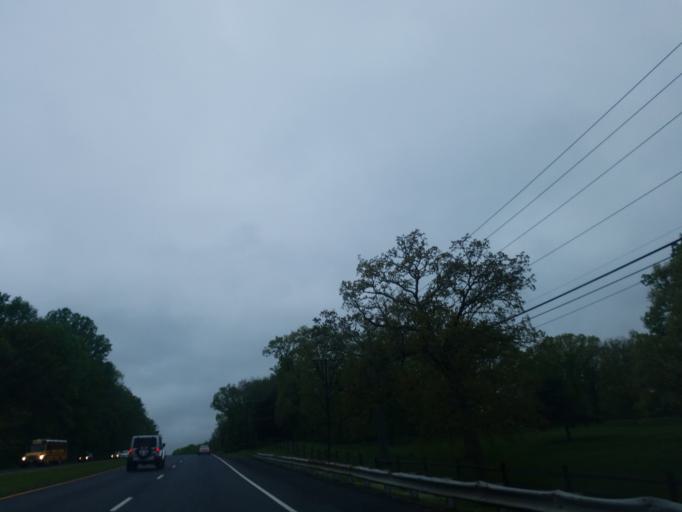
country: US
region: Virginia
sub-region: Fairfax County
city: Reston
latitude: 38.9745
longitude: -77.3242
